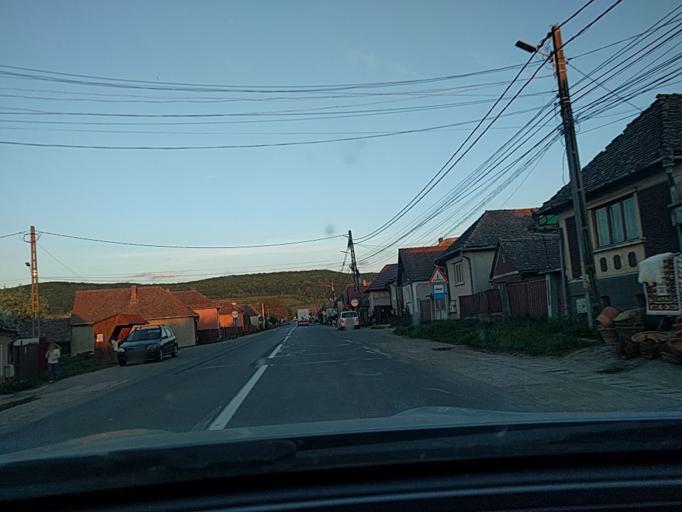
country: RO
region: Mures
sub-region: Comuna Balauseri
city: Chendu
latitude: 46.3942
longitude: 24.7221
